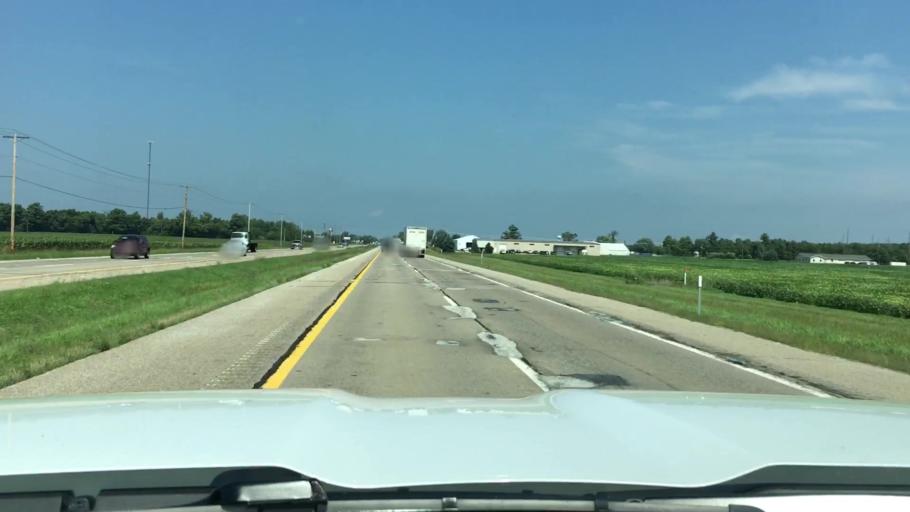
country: US
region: Michigan
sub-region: Kalamazoo County
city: Schoolcraft
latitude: 42.0858
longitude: -85.6366
